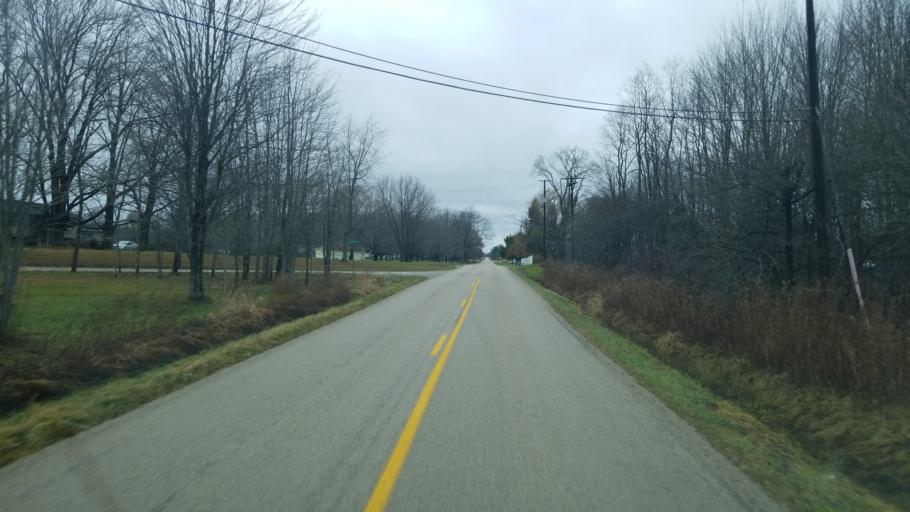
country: US
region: Ohio
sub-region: Ashtabula County
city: Jefferson
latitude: 41.7472
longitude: -80.6225
